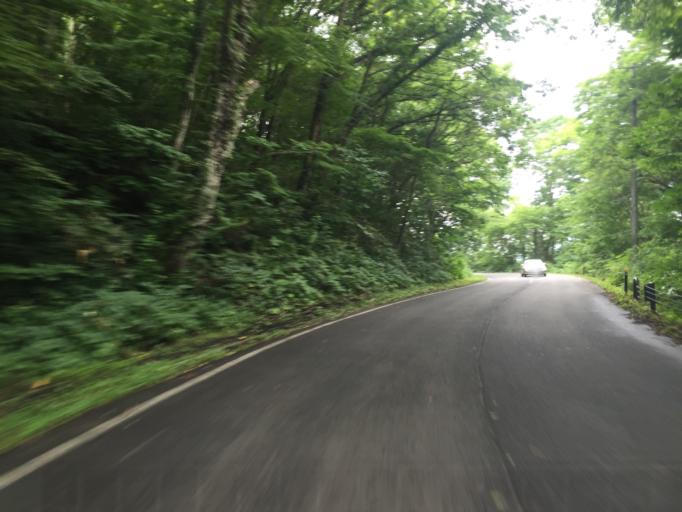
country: JP
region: Fukushima
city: Inawashiro
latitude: 37.7139
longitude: 140.0628
